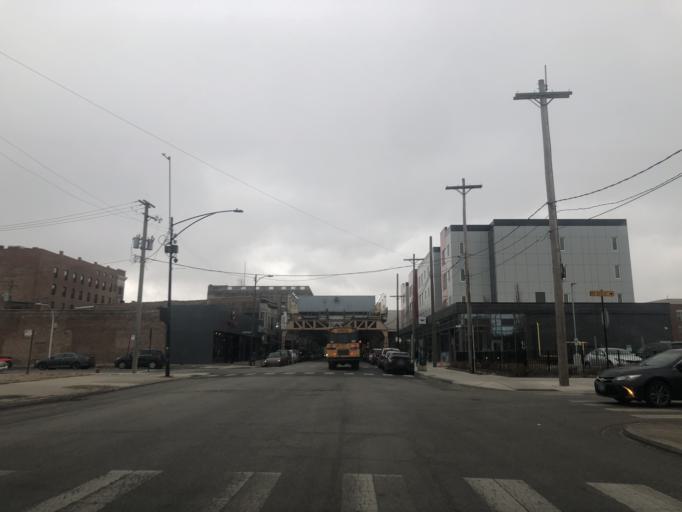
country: US
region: Illinois
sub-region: Cook County
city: Chicago
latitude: 41.7805
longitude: -87.6041
